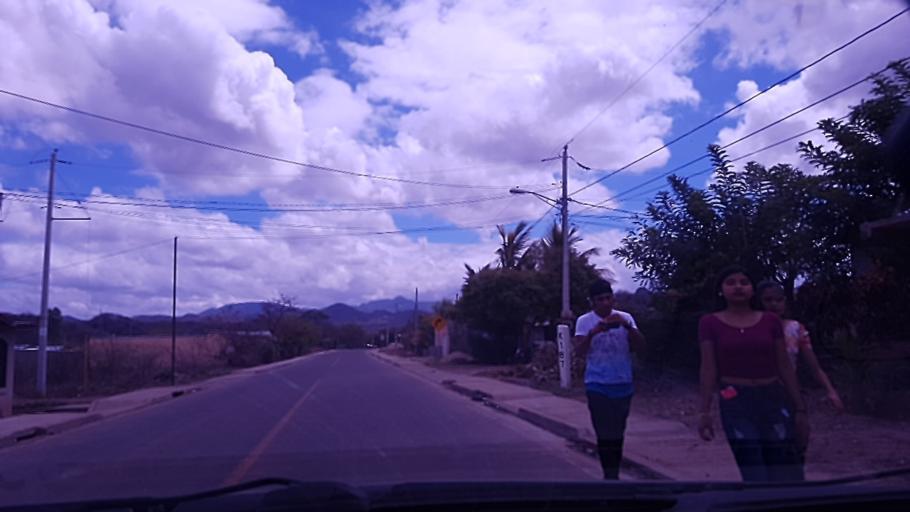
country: NI
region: Esteli
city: Condega
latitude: 13.3760
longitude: -86.3916
